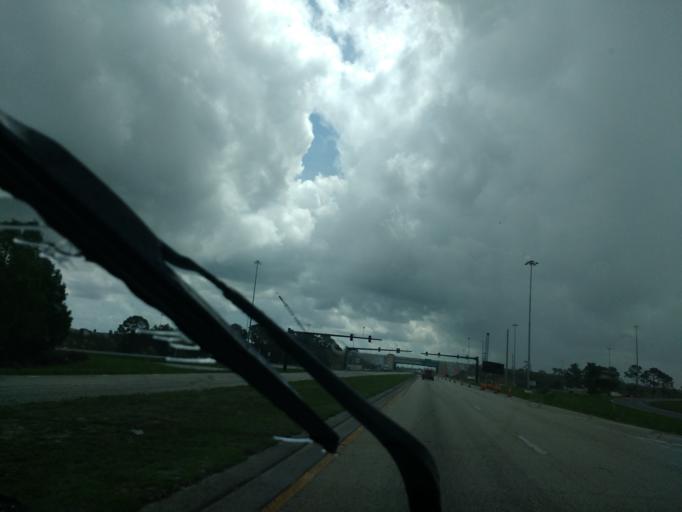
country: US
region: Florida
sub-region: Charlotte County
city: Charlotte Park
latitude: 26.8948
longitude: -82.0054
